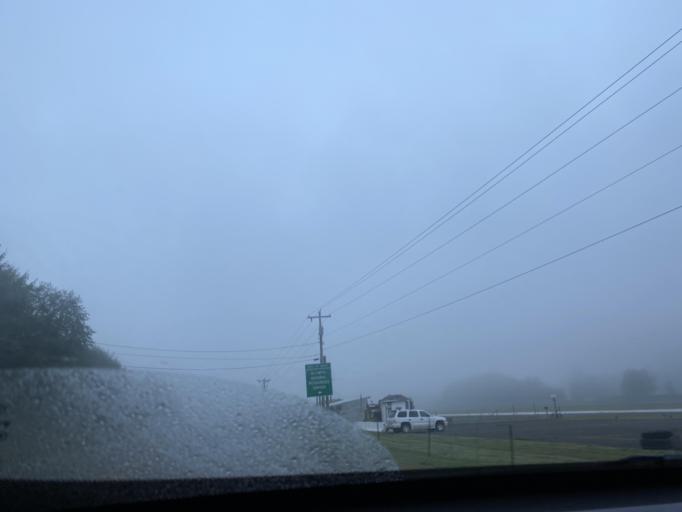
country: US
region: Washington
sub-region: Clallam County
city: Forks
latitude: 47.9368
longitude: -124.3949
